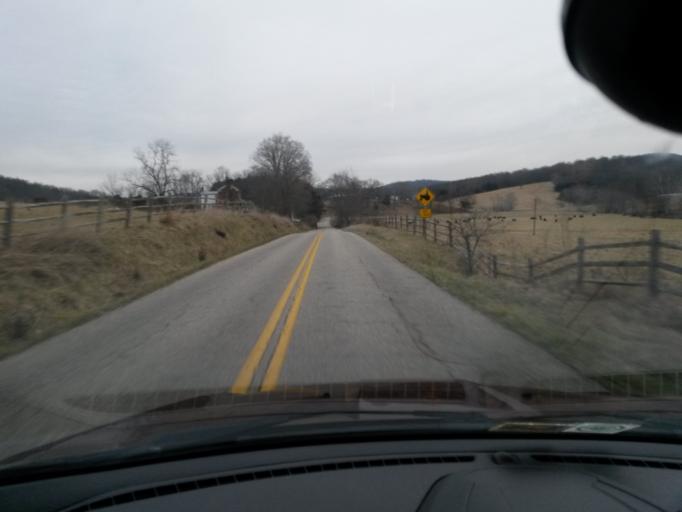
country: US
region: Virginia
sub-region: Rockbridge County
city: East Lexington
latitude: 37.9369
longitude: -79.3099
